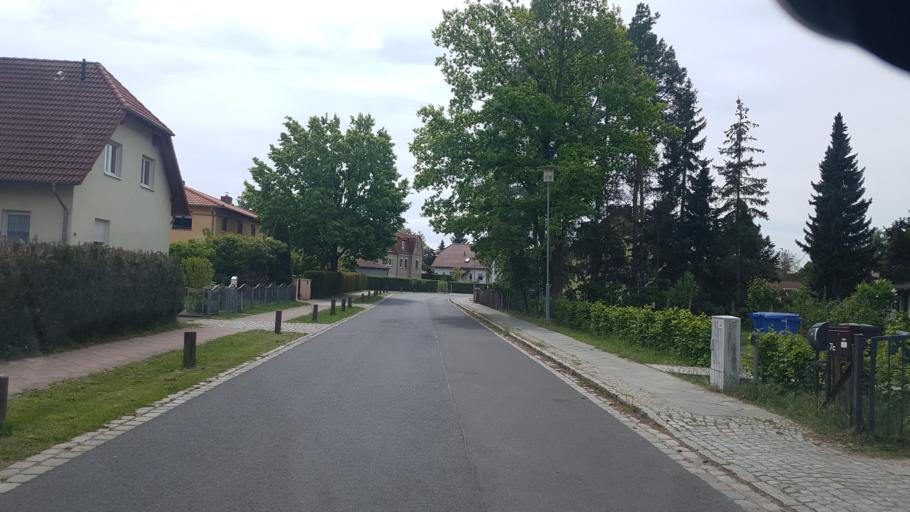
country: DE
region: Brandenburg
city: Michendorf
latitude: 52.2879
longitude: 13.0653
